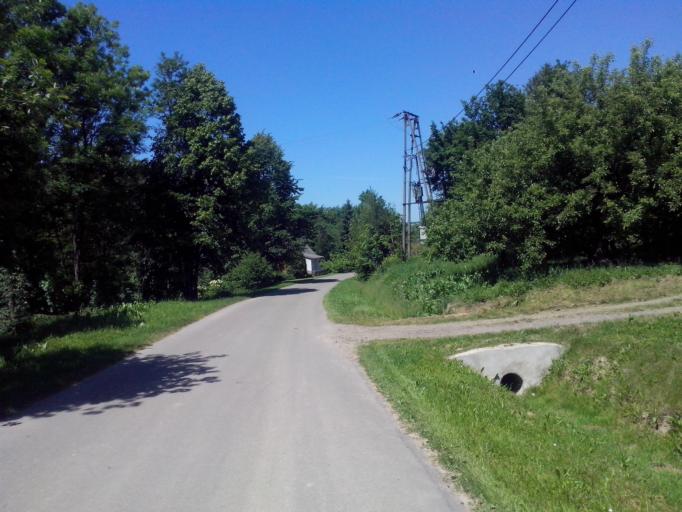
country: PL
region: Subcarpathian Voivodeship
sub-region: Powiat strzyzowski
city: Wisniowa
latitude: 49.8523
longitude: 21.6803
